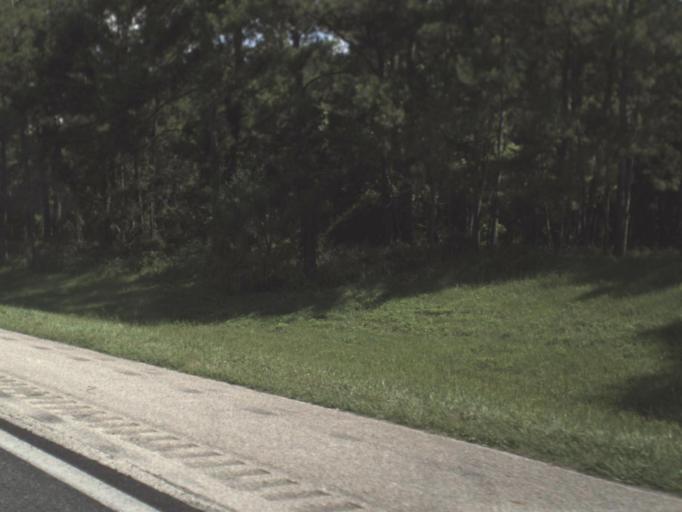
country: US
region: Florida
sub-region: Alachua County
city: Gainesville
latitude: 29.5314
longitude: -82.3175
